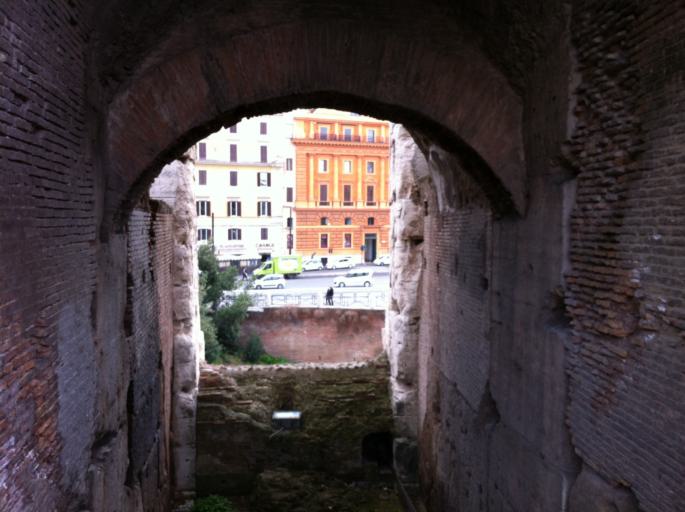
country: IT
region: Latium
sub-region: Citta metropolitana di Roma Capitale
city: Rome
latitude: 41.8899
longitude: 12.4930
